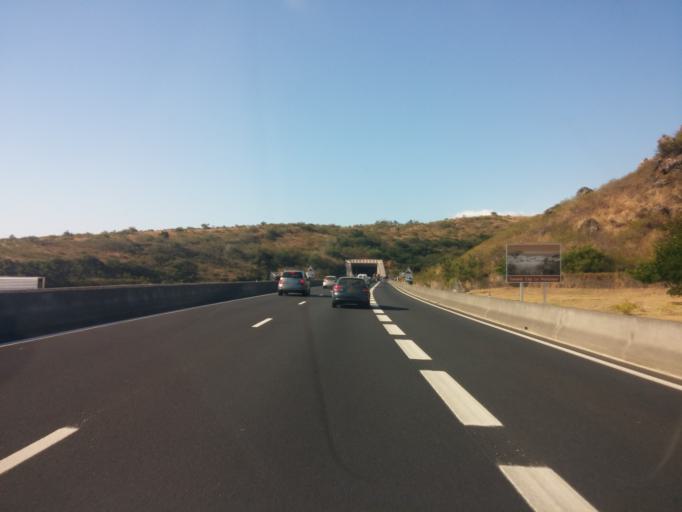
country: RE
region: Reunion
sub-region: Reunion
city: Saint-Paul
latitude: -21.0330
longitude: 55.2512
